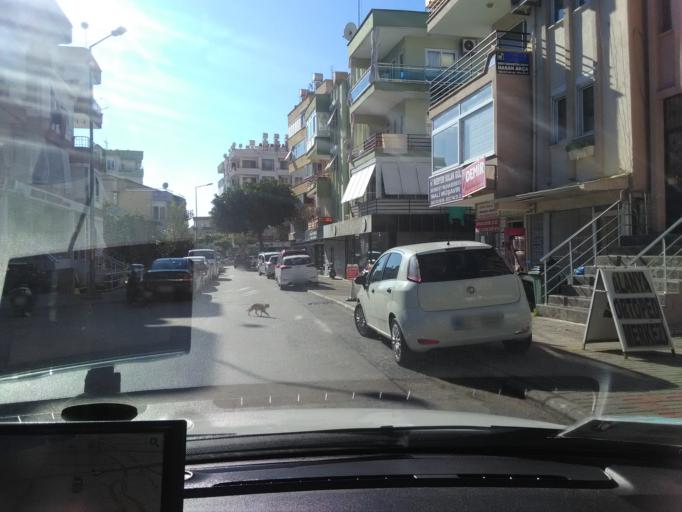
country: TR
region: Antalya
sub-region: Alanya
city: Alanya
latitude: 36.5480
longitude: 32.0002
